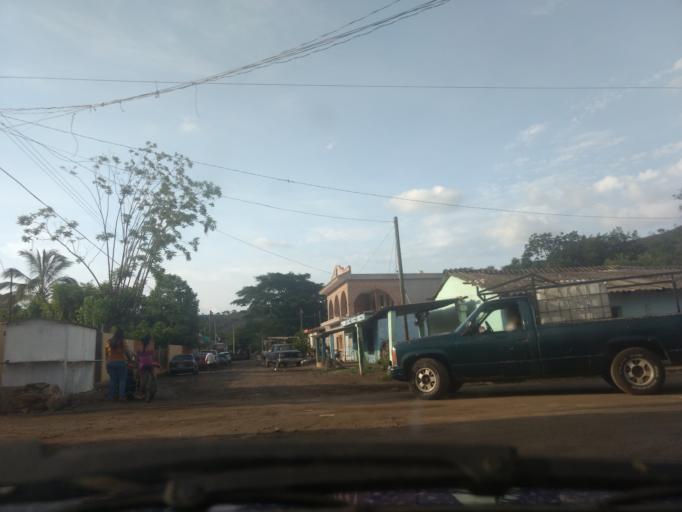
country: MX
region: Nayarit
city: Puga
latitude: 21.5280
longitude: -104.8045
